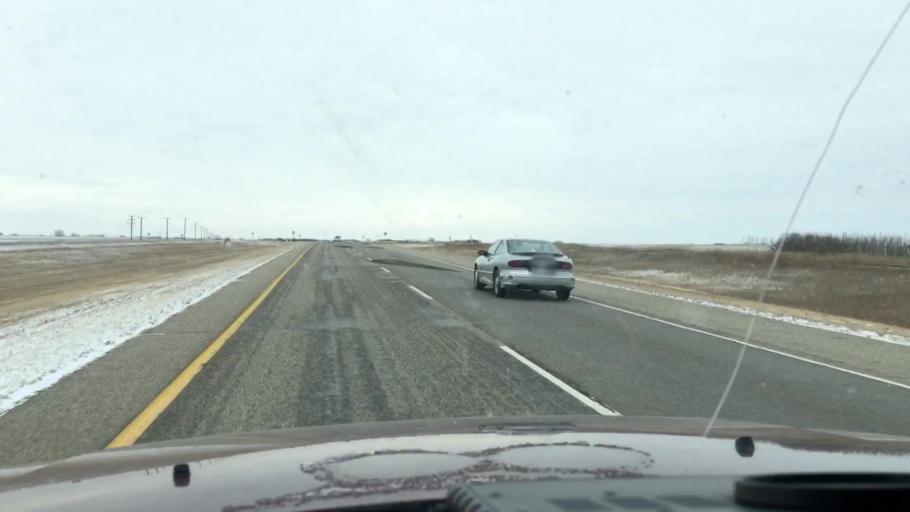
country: CA
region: Saskatchewan
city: Watrous
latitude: 51.4186
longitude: -106.1920
